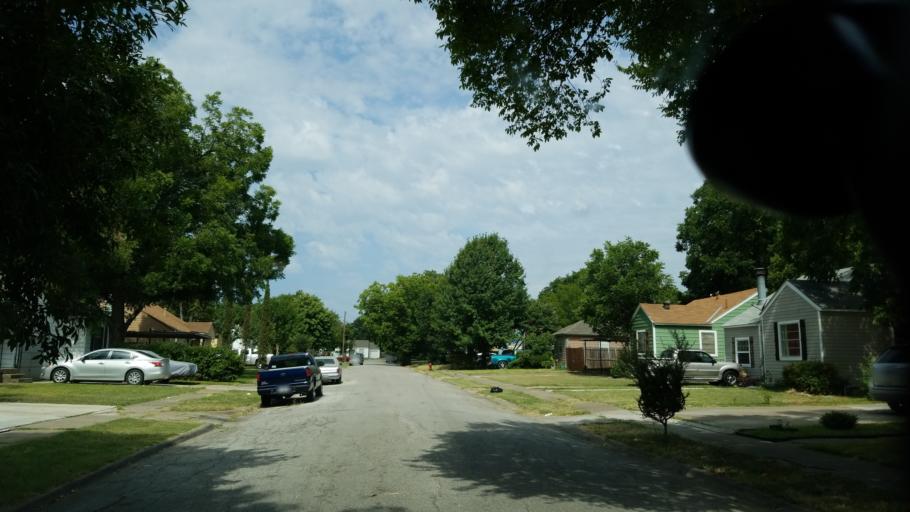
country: US
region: Texas
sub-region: Dallas County
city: Grand Prairie
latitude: 32.7525
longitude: -96.9888
